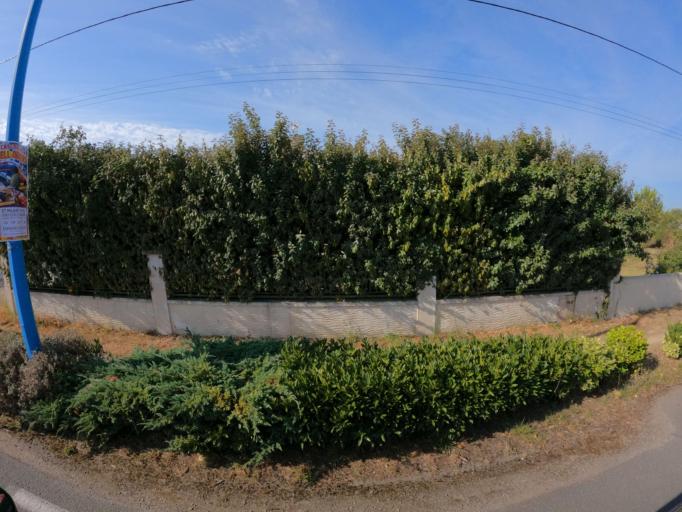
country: FR
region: Pays de la Loire
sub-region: Departement de la Vendee
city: Saint-Jean-de-Monts
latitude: 46.8053
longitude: -2.0954
